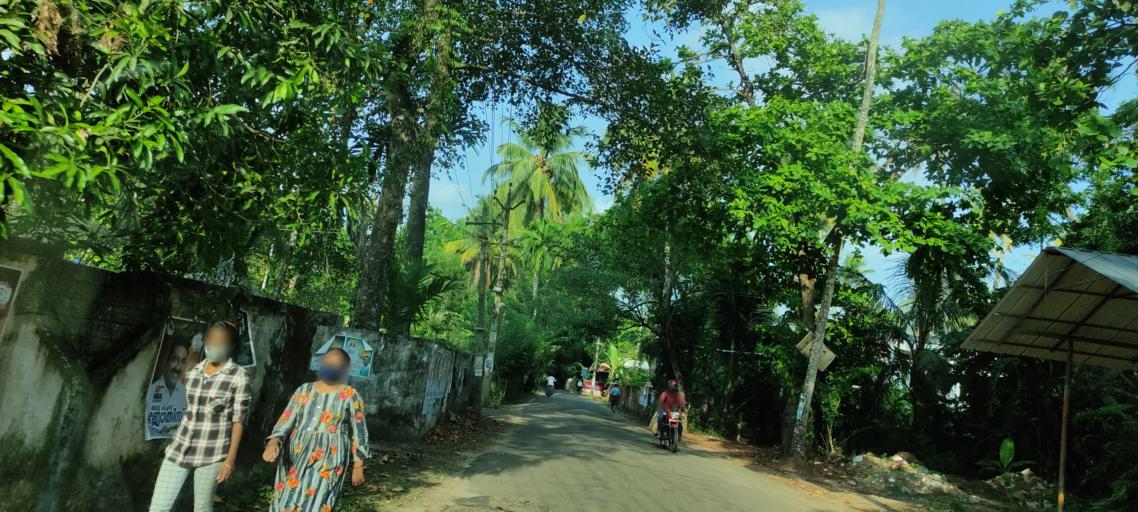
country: IN
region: Kerala
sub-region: Alappuzha
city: Vayalar
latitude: 9.7276
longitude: 76.2918
